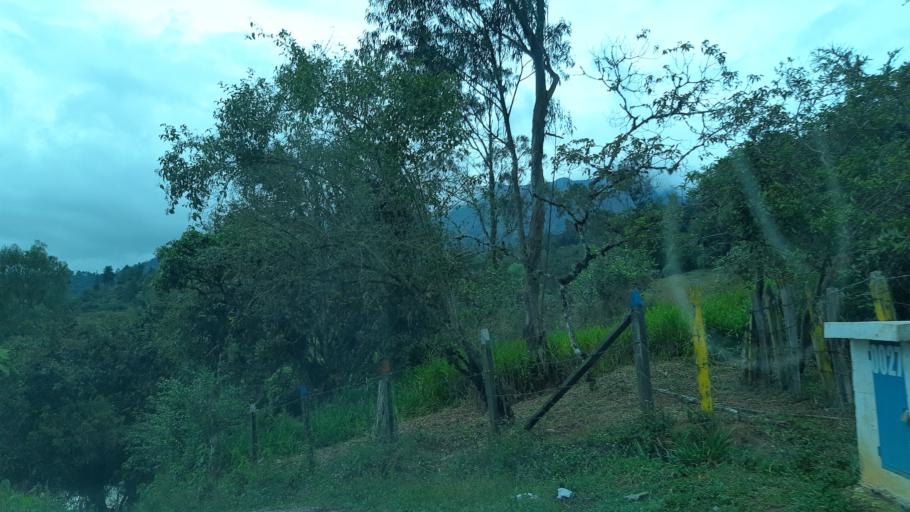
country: CO
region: Boyaca
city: Garagoa
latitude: 5.0847
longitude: -73.3552
